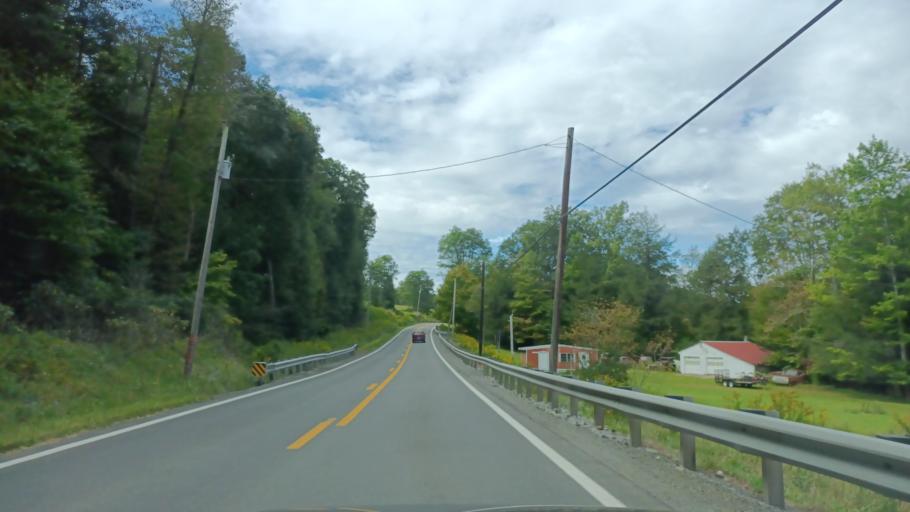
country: US
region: West Virginia
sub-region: Preston County
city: Terra Alta
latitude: 39.3272
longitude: -79.5172
